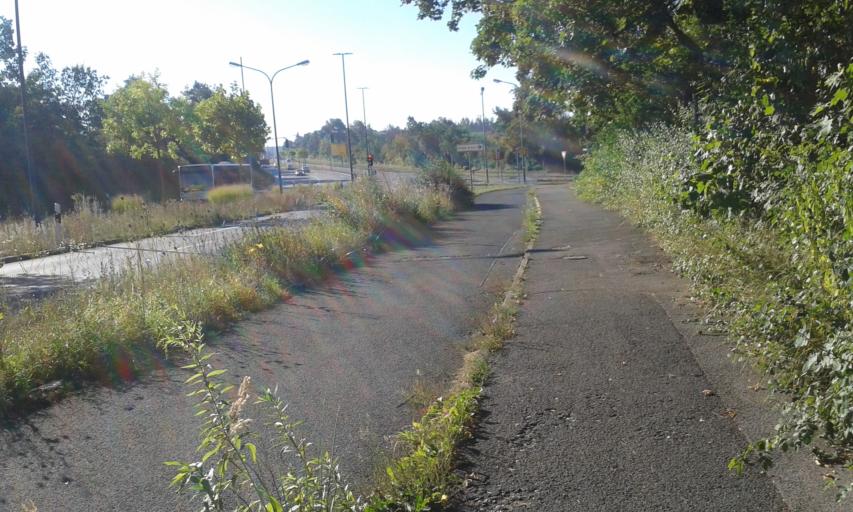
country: DE
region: Bavaria
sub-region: Upper Franconia
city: Bamberg
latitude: 49.8811
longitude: 10.9232
